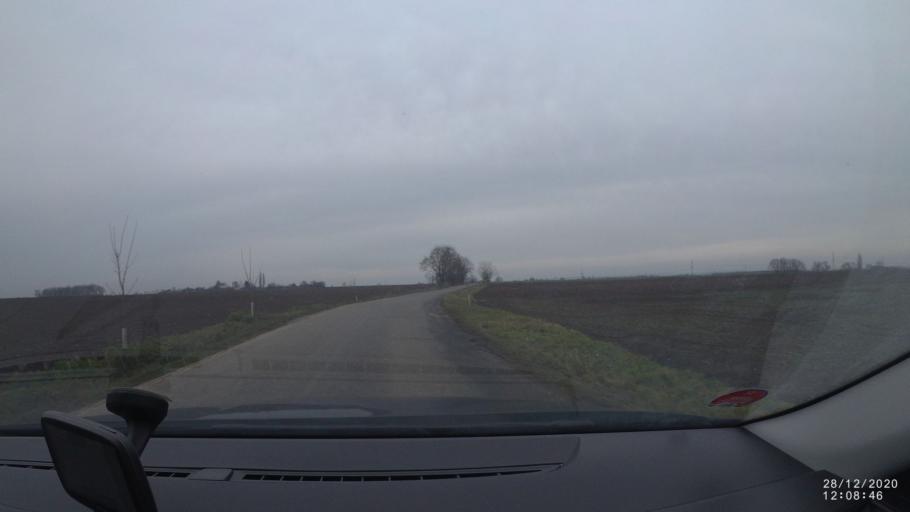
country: CZ
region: Central Bohemia
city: Zelenec
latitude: 50.1575
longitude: 14.6421
